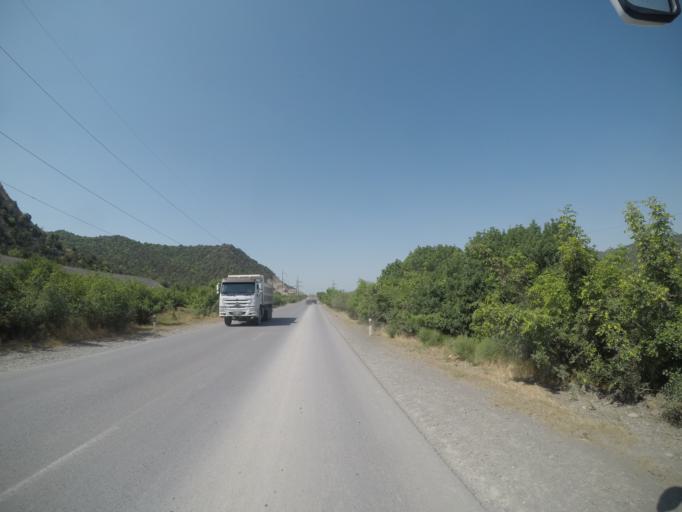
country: AZ
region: Agdas
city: Agdas
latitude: 40.7365
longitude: 47.5778
